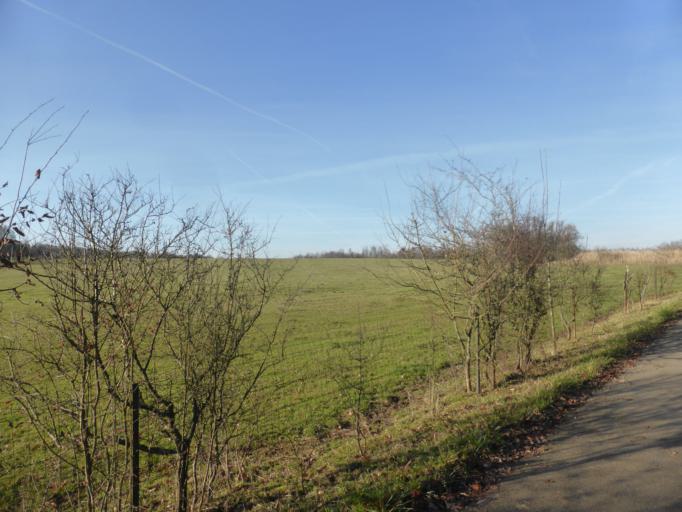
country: LU
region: Luxembourg
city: Hautcharage
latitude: 49.5893
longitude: 5.9109
